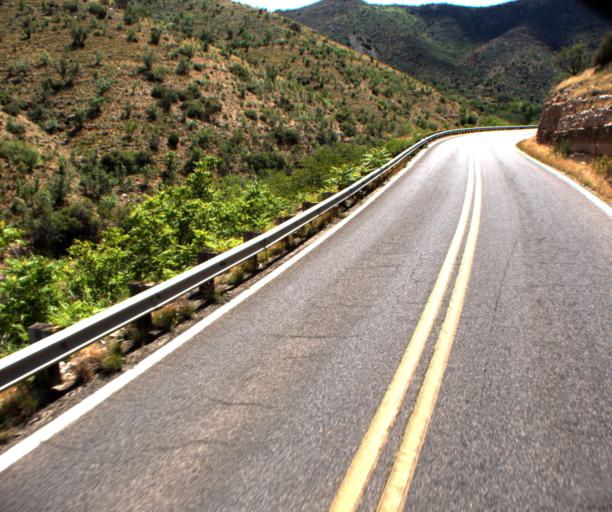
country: US
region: Arizona
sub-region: Yavapai County
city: Clarkdale
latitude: 34.7486
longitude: -112.1031
